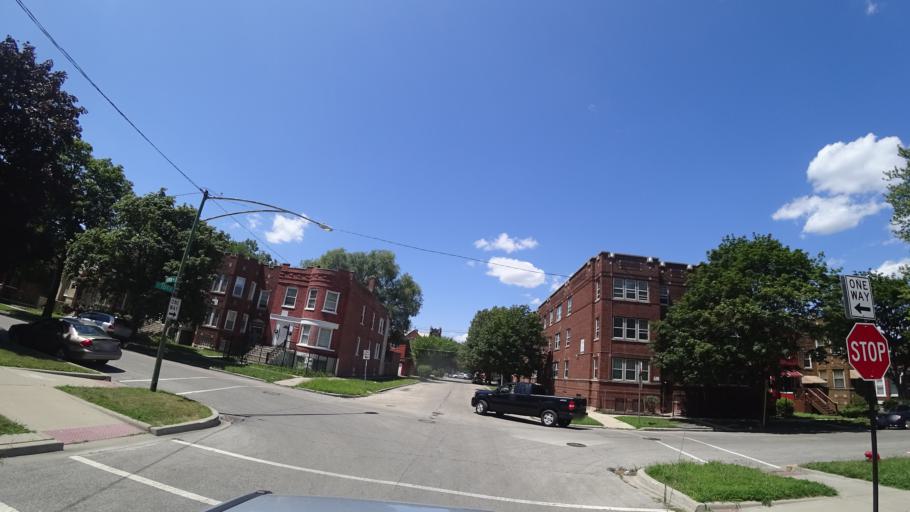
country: US
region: Illinois
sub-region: Cook County
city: Chicago
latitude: 41.7676
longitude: -87.6139
